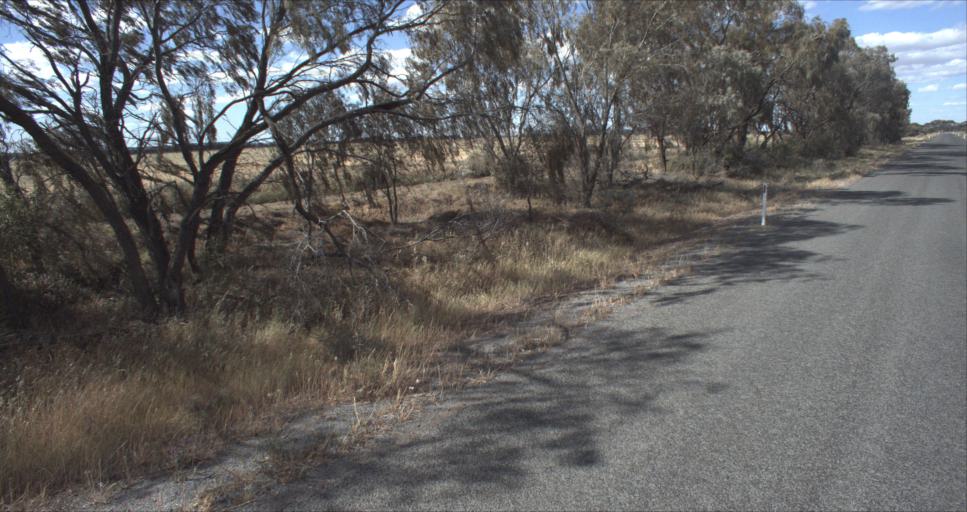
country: AU
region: New South Wales
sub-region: Leeton
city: Leeton
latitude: -34.4206
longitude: 146.2762
